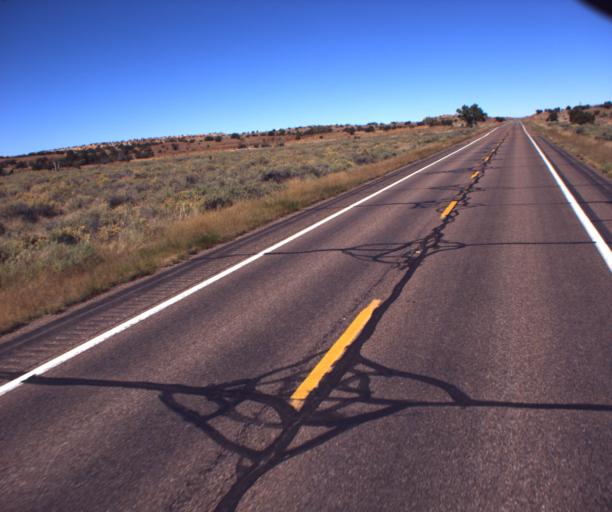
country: US
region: Arizona
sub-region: Apache County
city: Saint Johns
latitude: 34.3836
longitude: -109.4056
